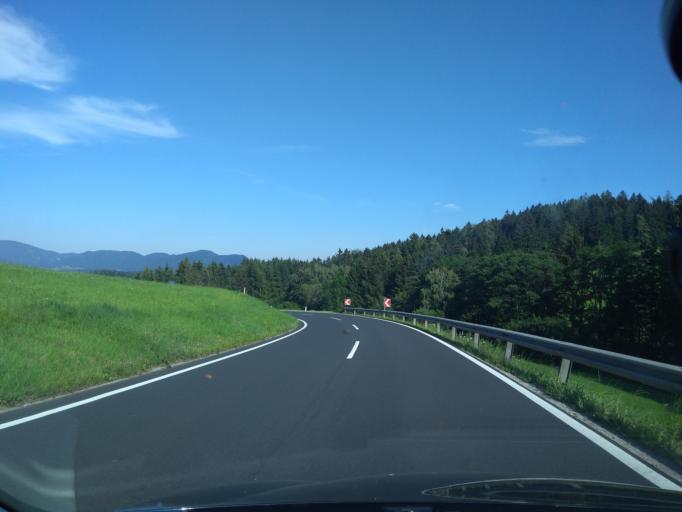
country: AT
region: Styria
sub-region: Politischer Bezirk Graz-Umgebung
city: Semriach
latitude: 47.2676
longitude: 15.4329
